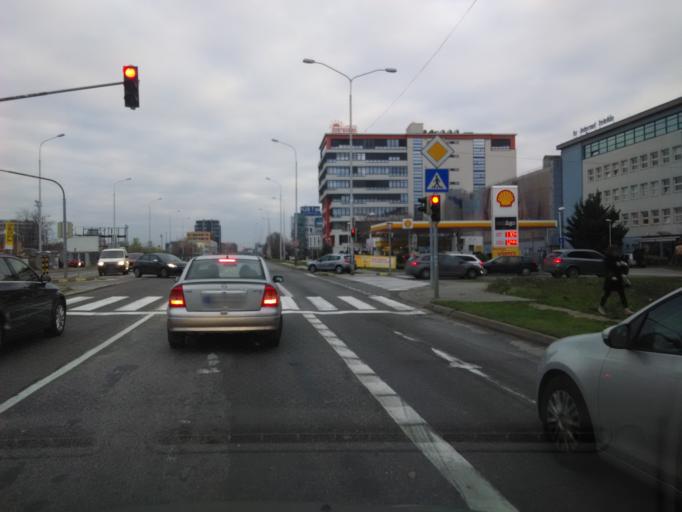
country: SK
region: Bratislavsky
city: Bratislava
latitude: 48.1186
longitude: 17.0986
